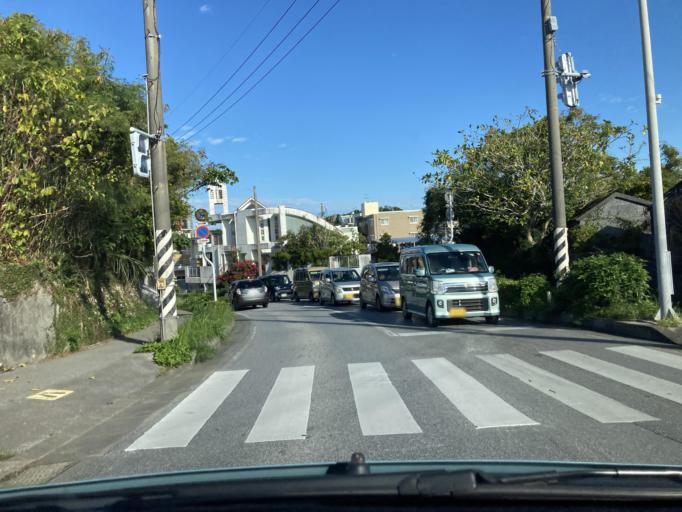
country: JP
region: Okinawa
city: Chatan
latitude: 26.3612
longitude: 127.7494
